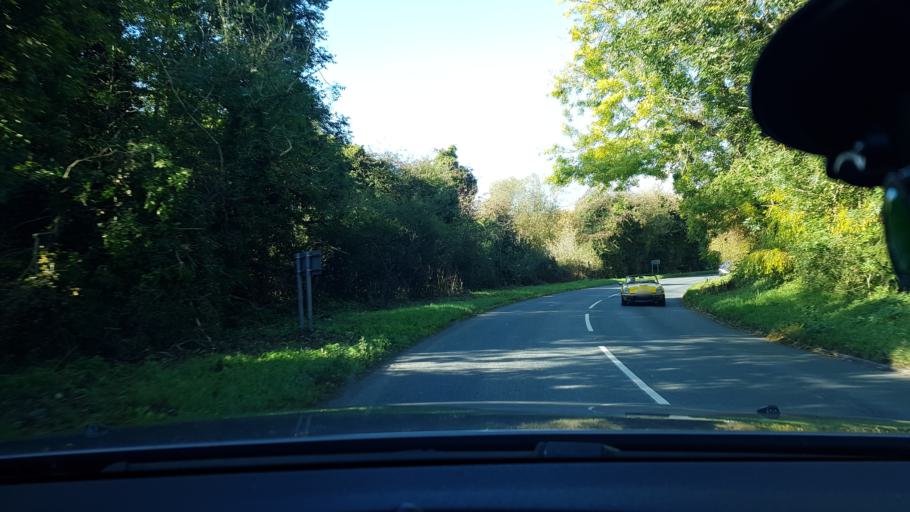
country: GB
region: England
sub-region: Wiltshire
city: Ramsbury
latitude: 51.4406
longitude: -1.5804
